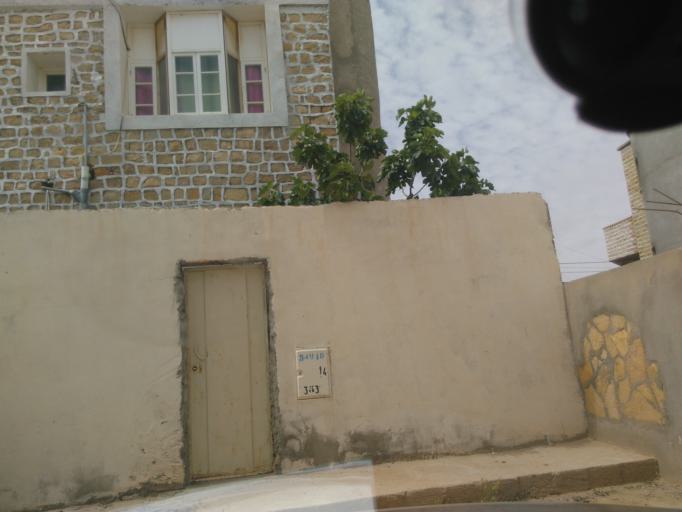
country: TN
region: Tataouine
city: Tataouine
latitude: 32.9491
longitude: 10.4706
